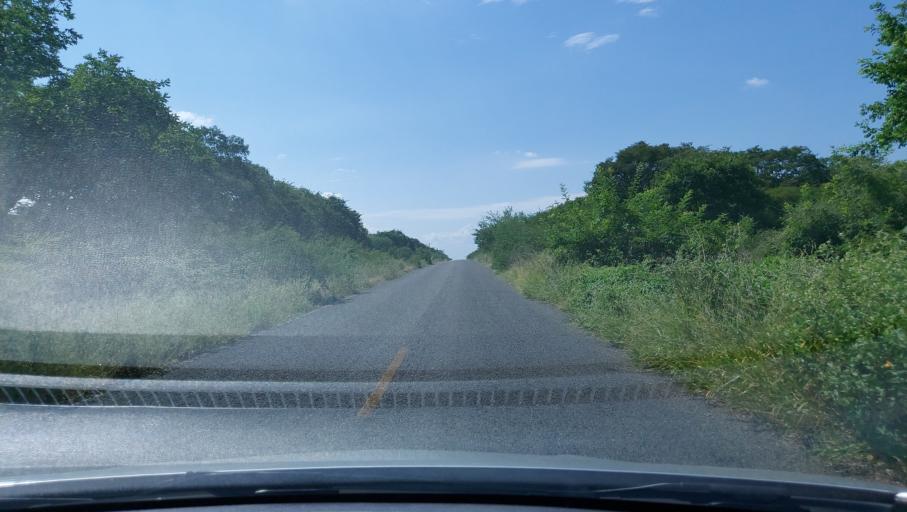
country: BR
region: Bahia
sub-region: Oliveira Dos Brejinhos
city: Beira Rio
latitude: -12.1751
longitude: -42.5441
